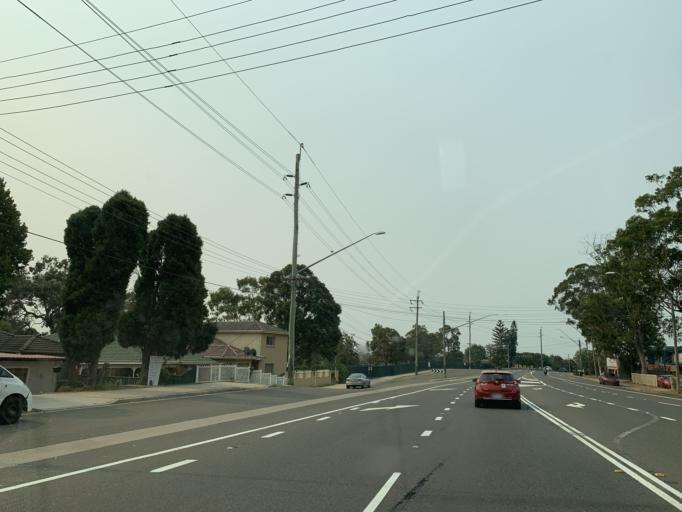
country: AU
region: New South Wales
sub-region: Blacktown
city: Blacktown
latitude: -33.7906
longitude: 150.9191
